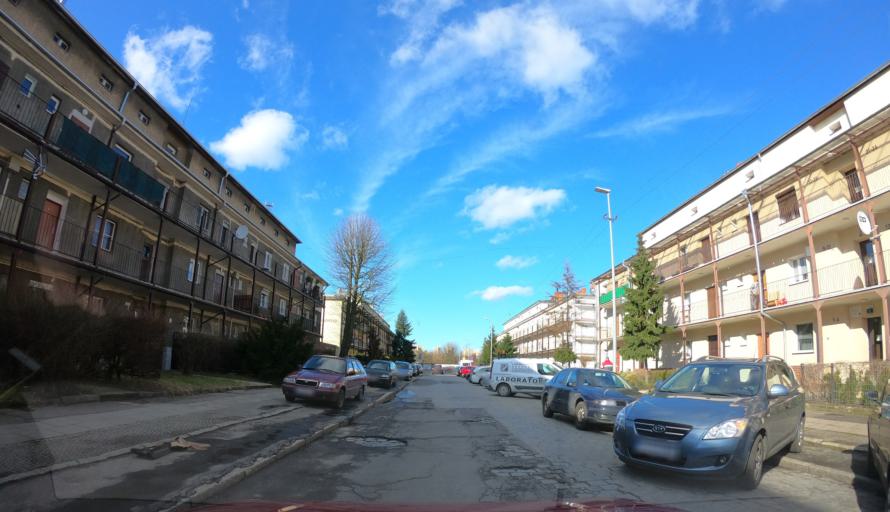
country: PL
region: West Pomeranian Voivodeship
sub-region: Szczecin
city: Szczecin
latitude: 53.4227
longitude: 14.5147
